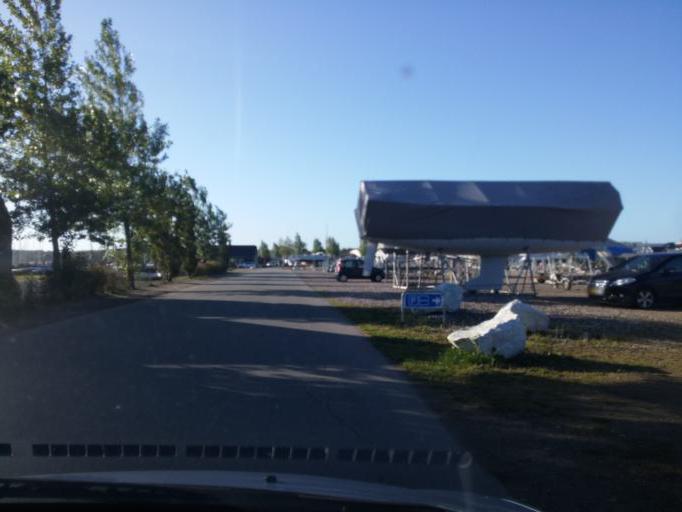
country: DK
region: South Denmark
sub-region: Kerteminde Kommune
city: Kerteminde
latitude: 55.4536
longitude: 10.6645
